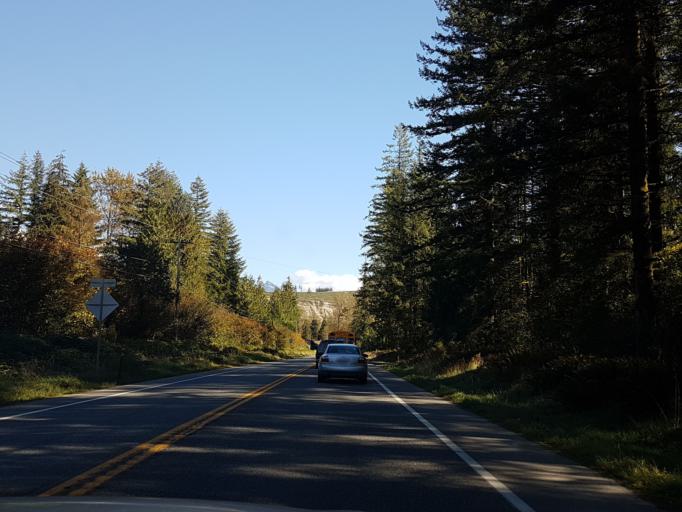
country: US
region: Washington
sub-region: Snohomish County
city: Gold Bar
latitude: 47.8359
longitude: -121.6529
